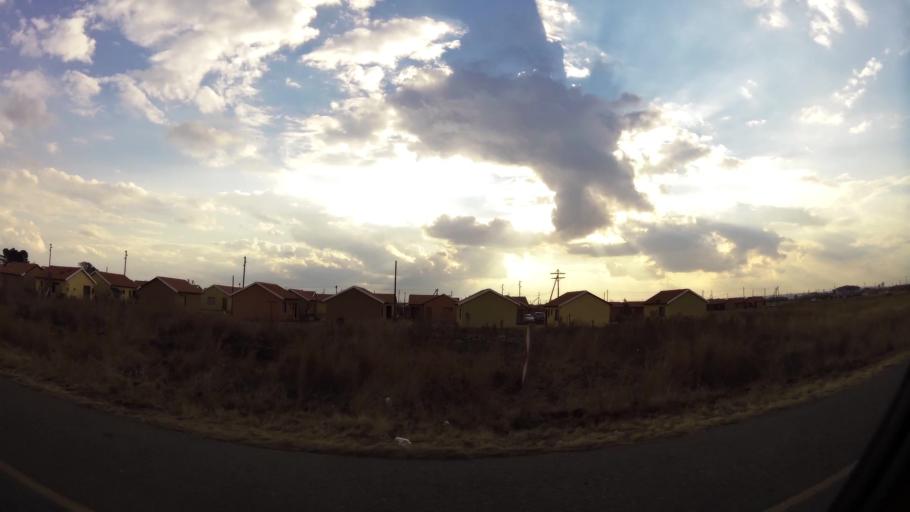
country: ZA
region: Gauteng
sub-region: Sedibeng District Municipality
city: Vanderbijlpark
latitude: -26.6161
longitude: 27.8134
